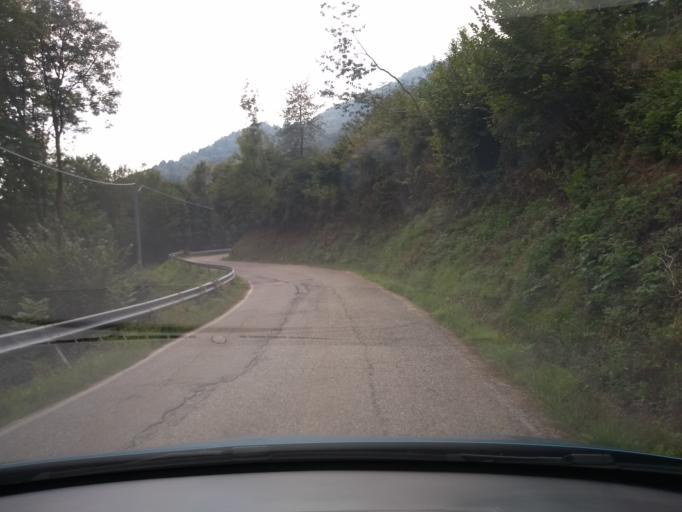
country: IT
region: Piedmont
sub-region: Provincia di Torino
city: Corio
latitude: 45.3341
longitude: 7.5175
